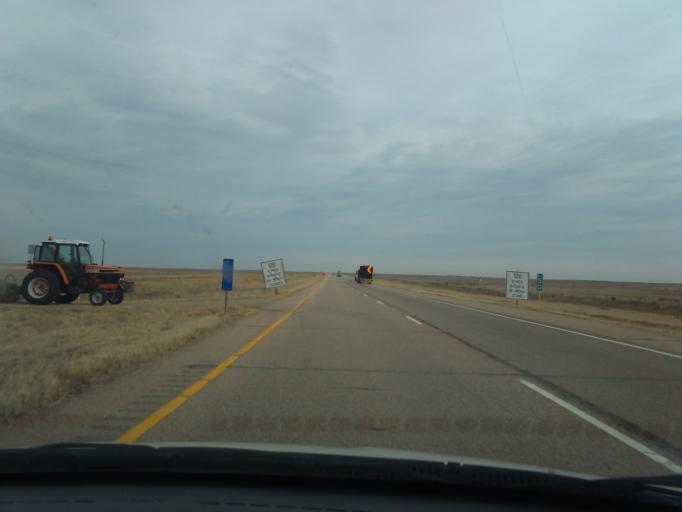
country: US
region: Colorado
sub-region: Weld County
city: Keenesburg
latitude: 40.1723
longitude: -104.3393
